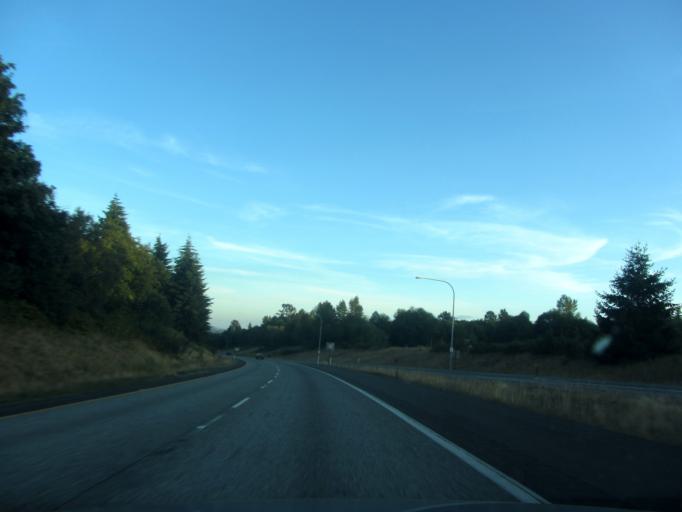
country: US
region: Washington
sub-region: Skagit County
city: Burlington
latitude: 48.5362
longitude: -122.3539
